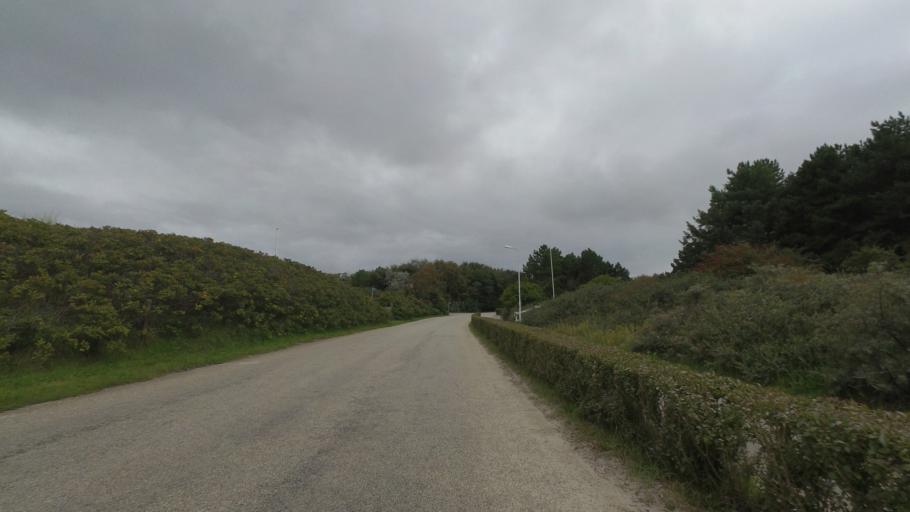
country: NL
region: Friesland
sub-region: Gemeente Ameland
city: Nes
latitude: 53.4591
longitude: 5.8072
